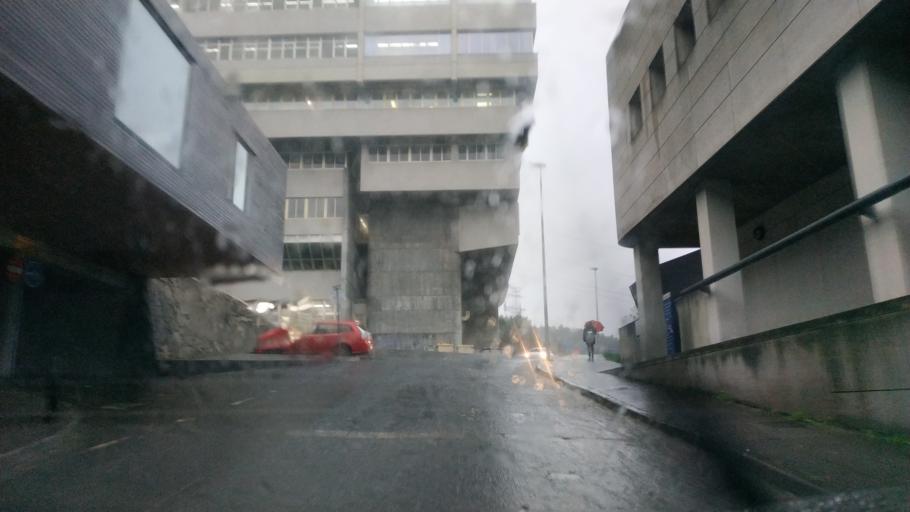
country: ES
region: Galicia
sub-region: Provincia da Coruna
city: Culleredo
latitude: 43.3279
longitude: -8.4091
